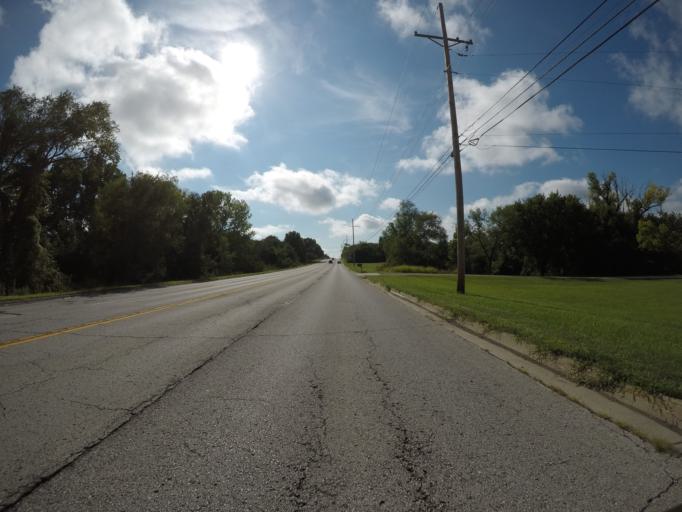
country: US
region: Kansas
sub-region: Leavenworth County
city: Basehor
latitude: 39.1287
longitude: -94.8879
